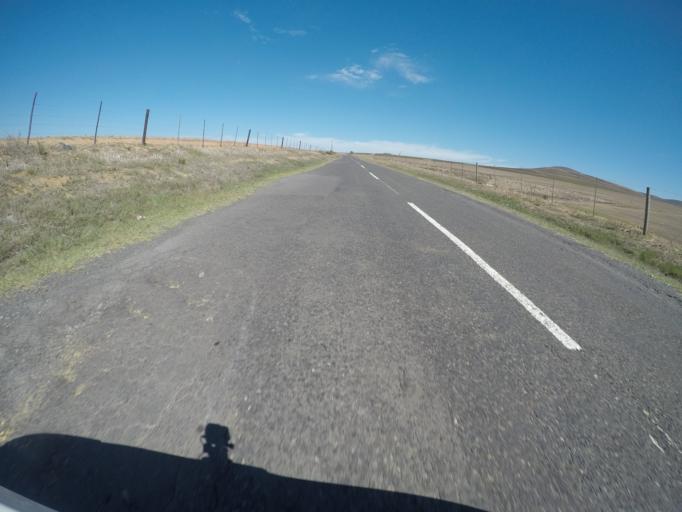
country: ZA
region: Western Cape
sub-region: City of Cape Town
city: Atlantis
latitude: -33.7022
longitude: 18.5874
